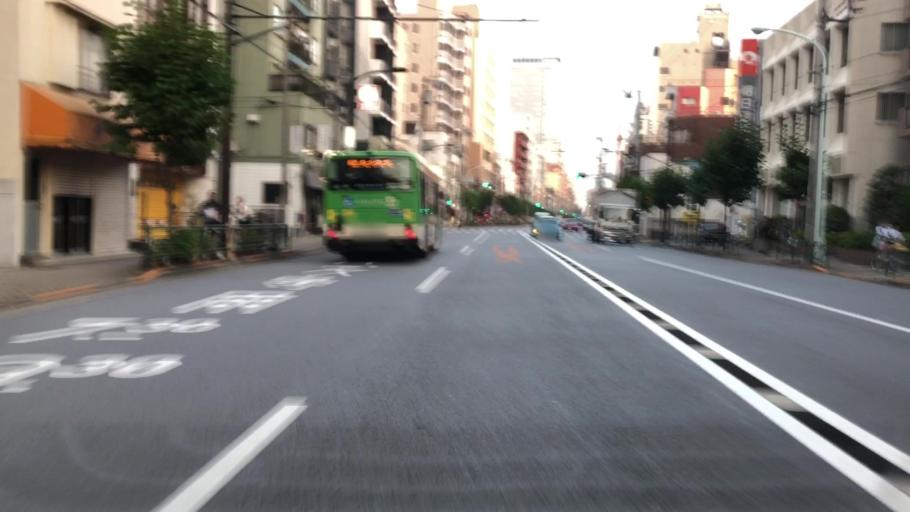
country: JP
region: Tokyo
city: Urayasu
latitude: 35.7074
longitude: 139.8140
